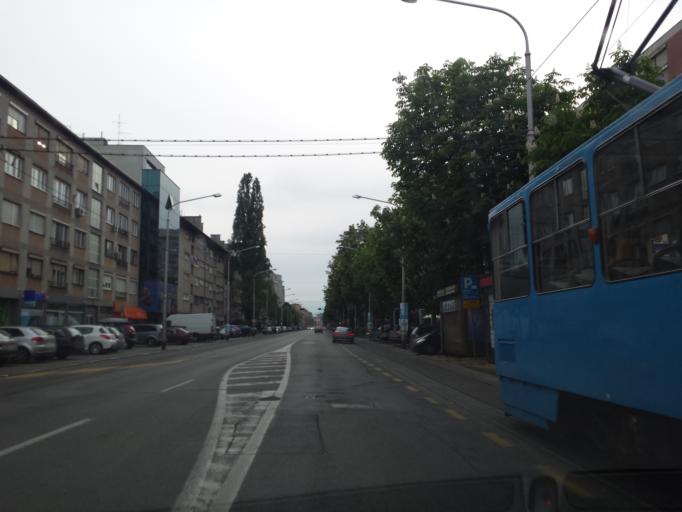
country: HR
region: Grad Zagreb
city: Zagreb
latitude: 45.8186
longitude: 16.0122
